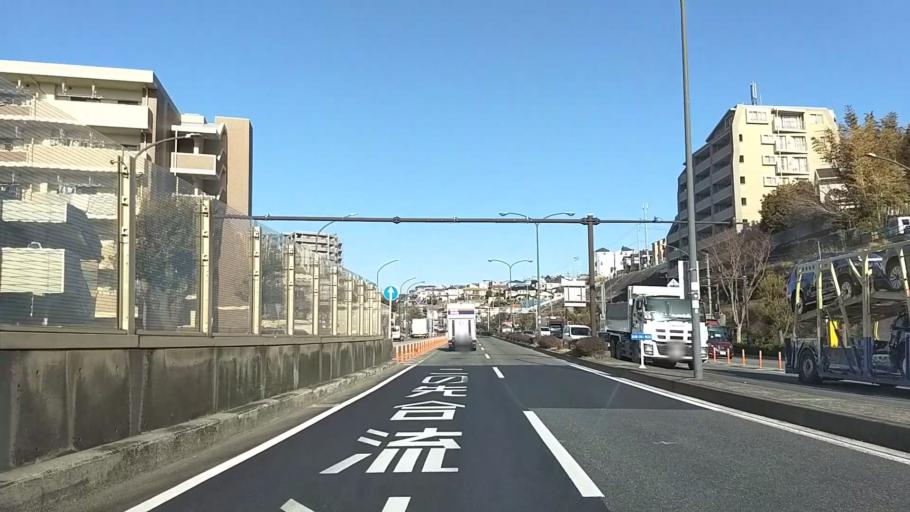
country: JP
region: Kanagawa
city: Yokohama
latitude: 35.3970
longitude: 139.5821
